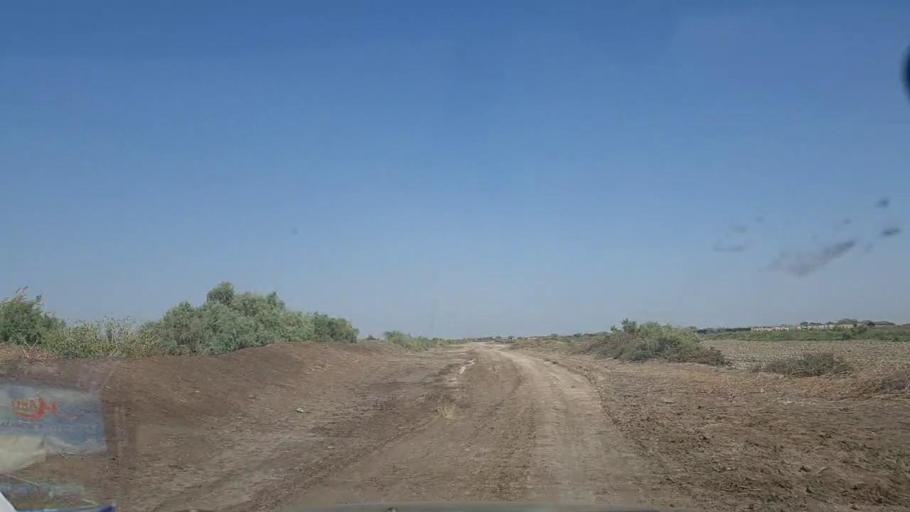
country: PK
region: Sindh
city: Chuhar Jamali
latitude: 24.2719
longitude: 67.7523
